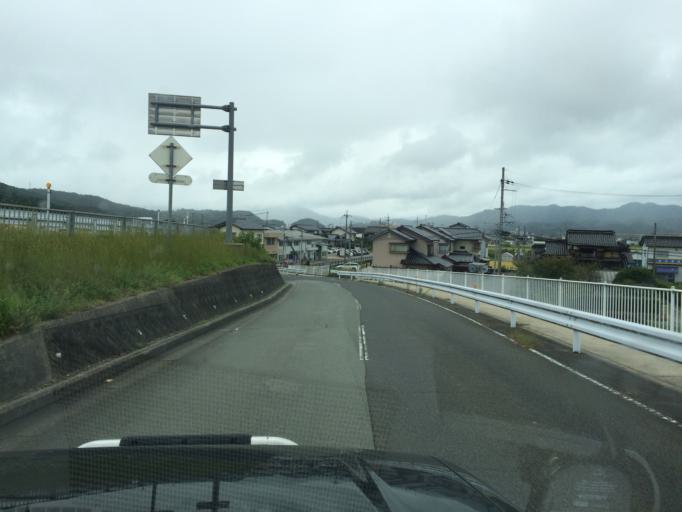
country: JP
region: Hyogo
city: Toyooka
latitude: 35.5140
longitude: 134.8264
